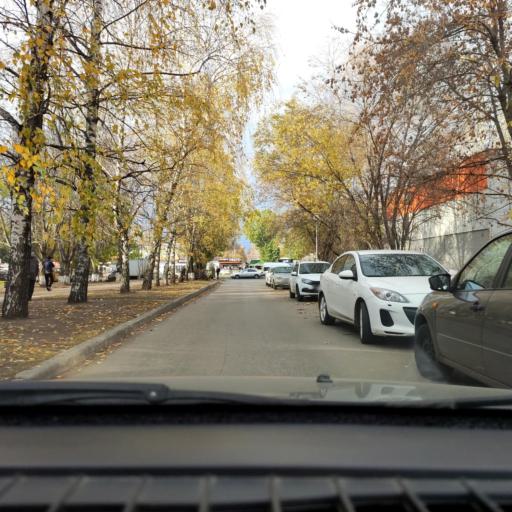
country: RU
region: Samara
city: Tol'yatti
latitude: 53.5079
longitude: 49.2938
